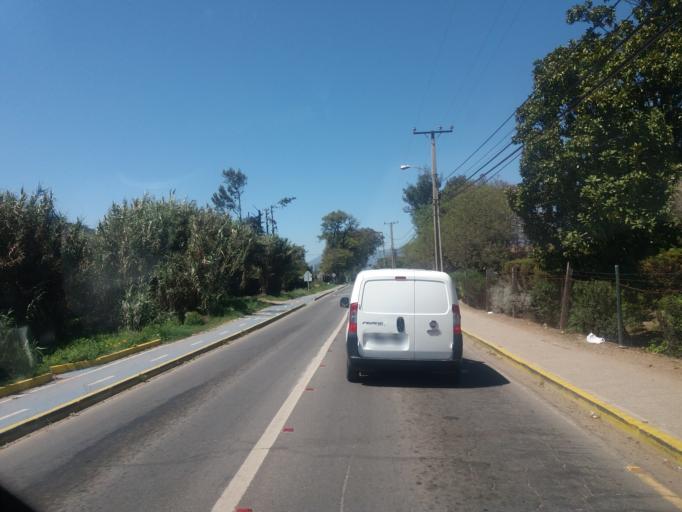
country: CL
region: Valparaiso
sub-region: Provincia de Marga Marga
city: Limache
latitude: -32.9808
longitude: -71.2817
